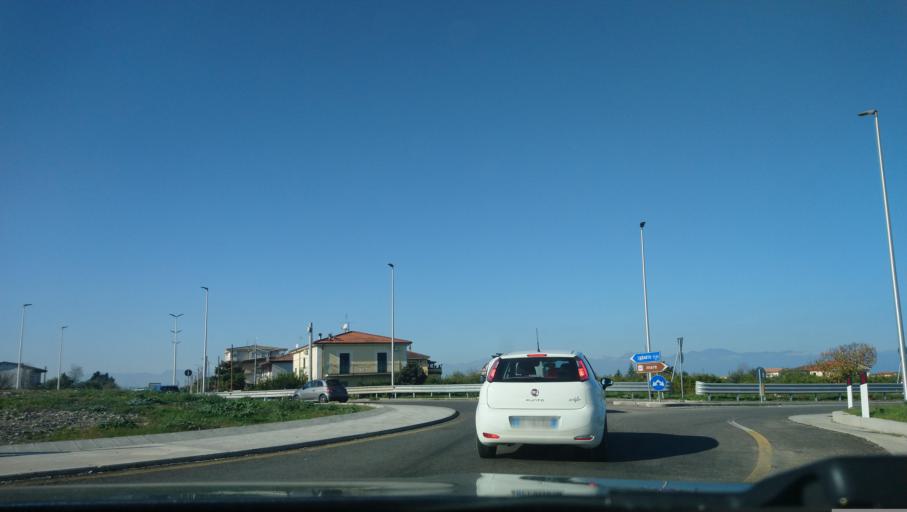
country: IT
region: Calabria
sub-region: Provincia di Cosenza
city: Fabrizio
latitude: 39.6319
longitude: 16.5652
